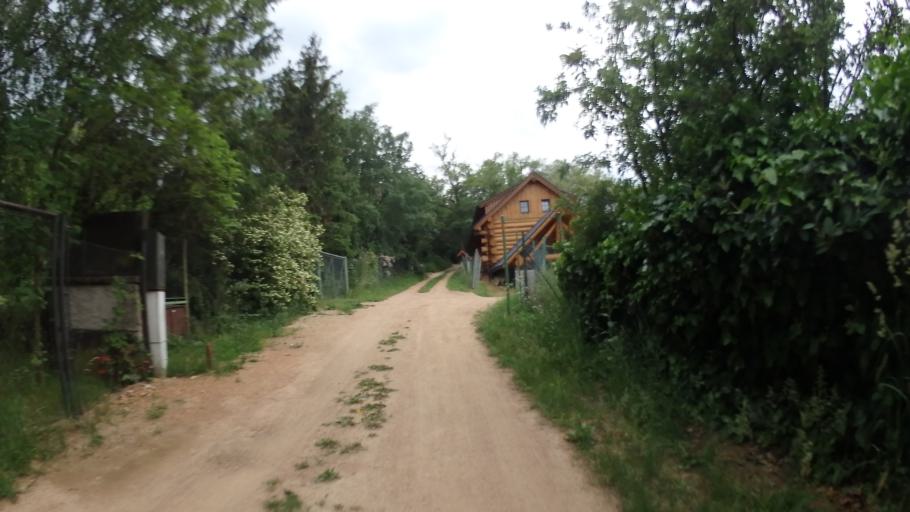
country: CZ
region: South Moravian
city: Ostopovice
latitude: 49.1370
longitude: 16.5437
